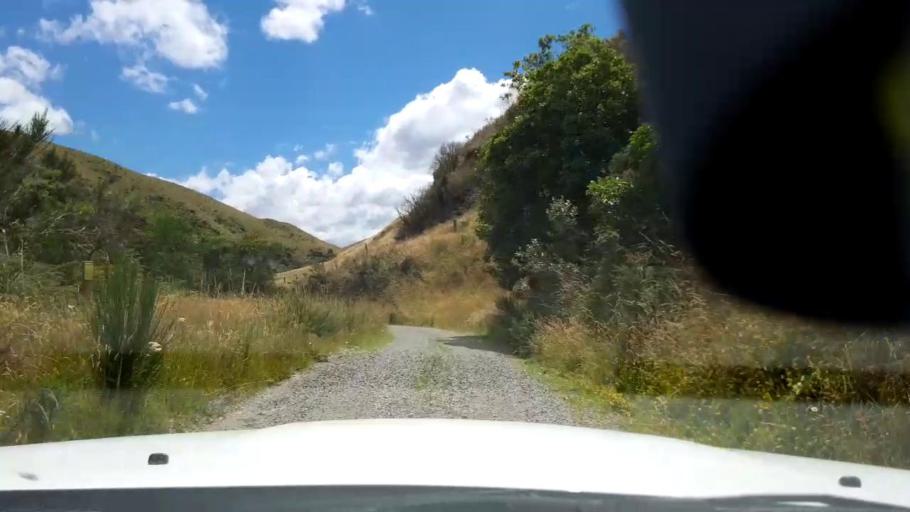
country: NZ
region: Canterbury
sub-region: Timaru District
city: Pleasant Point
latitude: -43.9333
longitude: 171.1975
